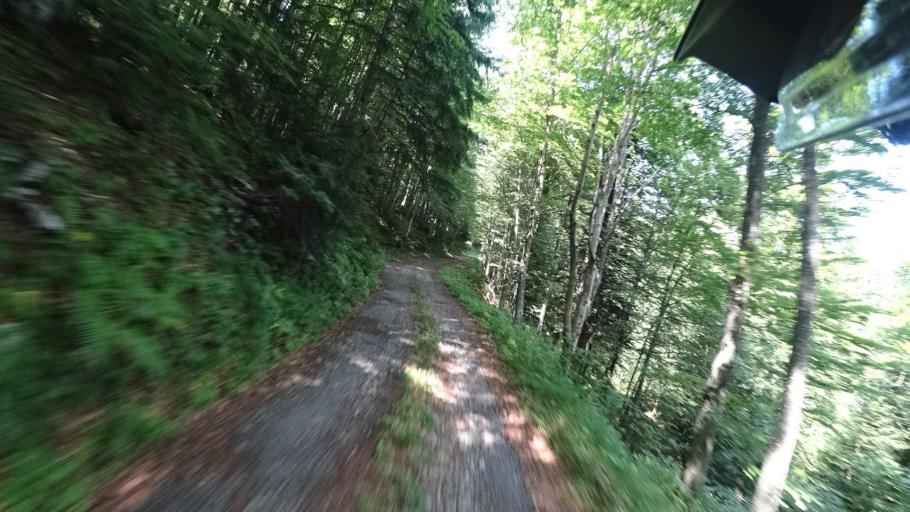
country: HR
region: Primorsko-Goranska
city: Vrbovsko
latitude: 45.3282
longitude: 15.0294
